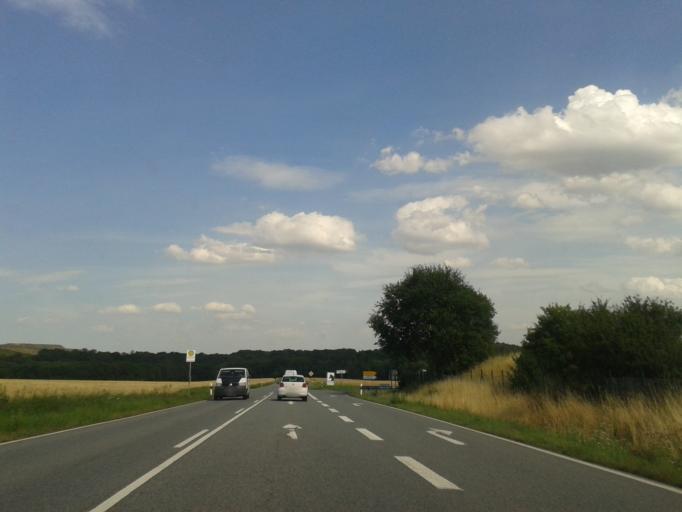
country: DE
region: Saxony
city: Reinsberg
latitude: 51.0525
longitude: 13.3723
